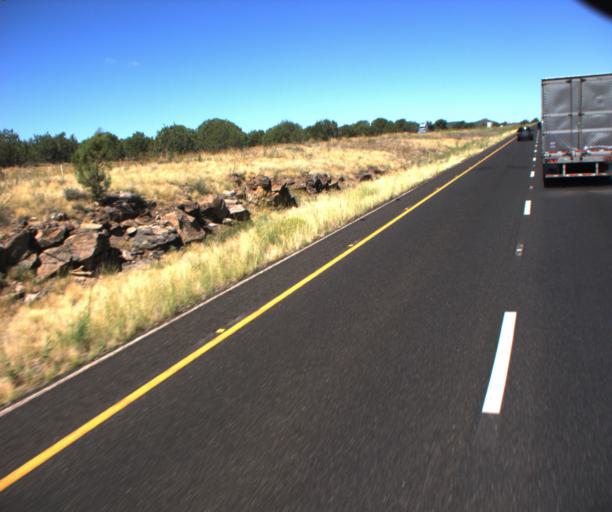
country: US
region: Arizona
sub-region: Yavapai County
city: Paulden
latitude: 35.2558
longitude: -112.7055
